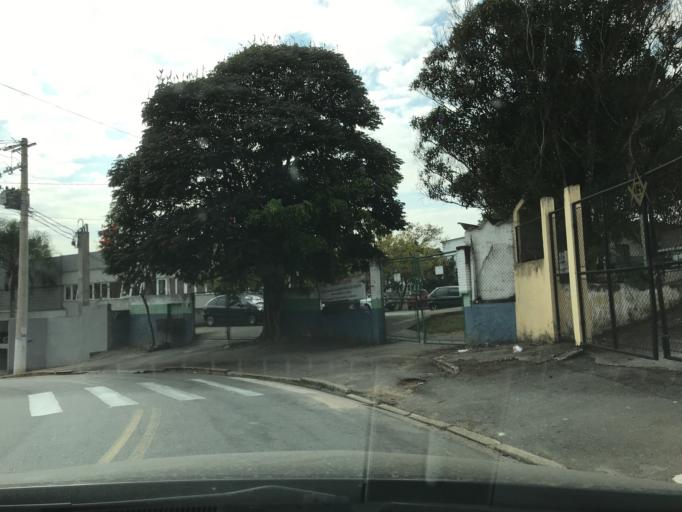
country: BR
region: Sao Paulo
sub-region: Cotia
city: Cotia
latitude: -23.6053
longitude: -46.9128
